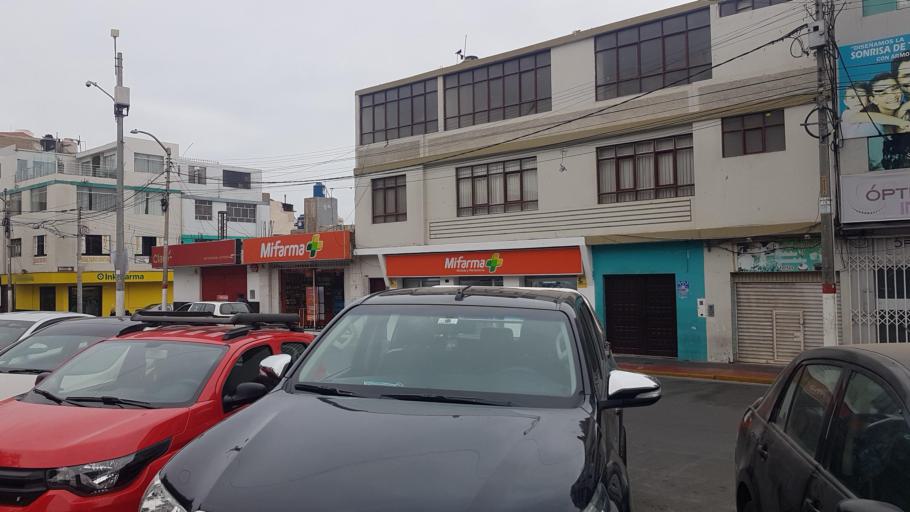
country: PE
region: Moquegua
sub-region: Provincia de Ilo
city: Ilo
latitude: -17.6475
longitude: -71.3444
